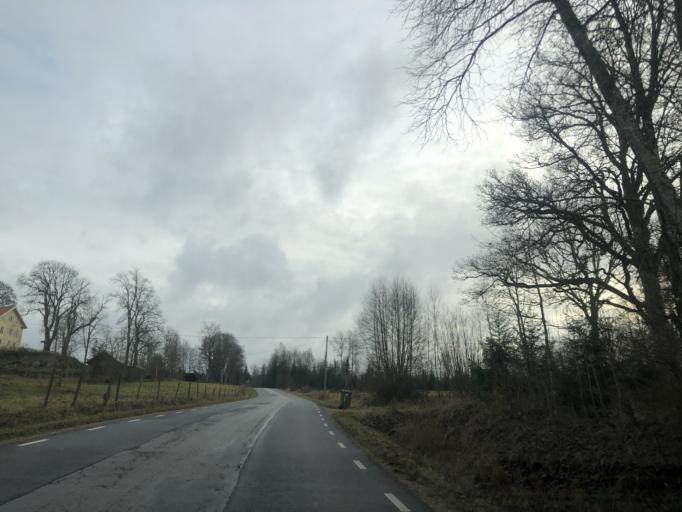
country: SE
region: Vaestra Goetaland
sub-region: Boras Kommun
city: Dalsjofors
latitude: 57.8240
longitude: 13.1927
